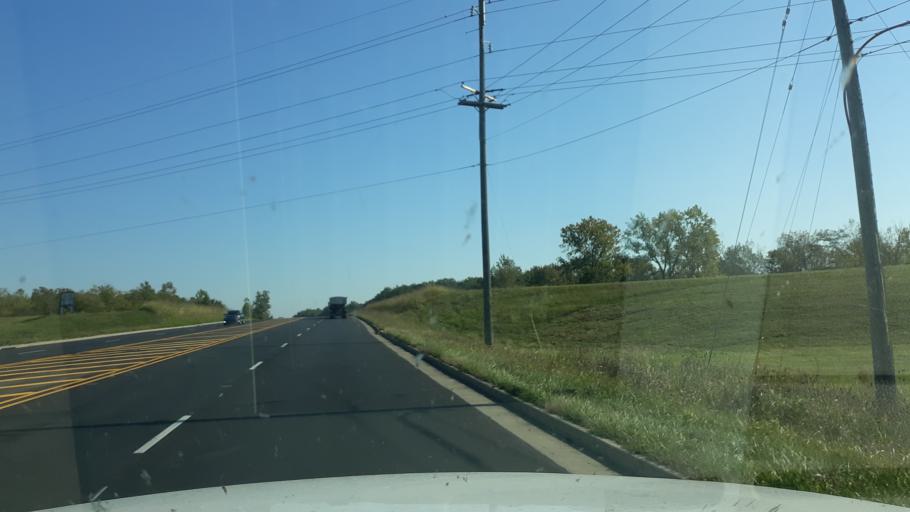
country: US
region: Illinois
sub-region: Saline County
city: Harrisburg
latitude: 37.7467
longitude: -88.5237
